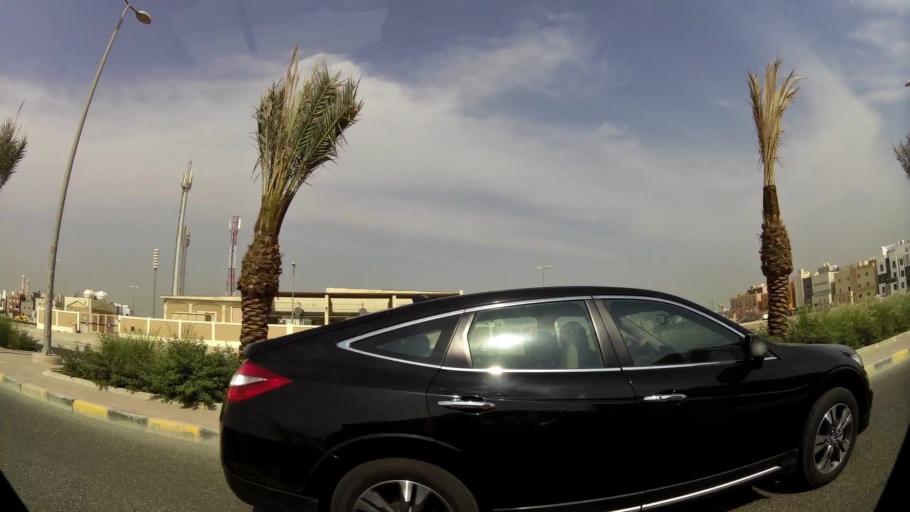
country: KW
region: Al Farwaniyah
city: Janub as Surrah
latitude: 29.2904
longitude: 47.9992
